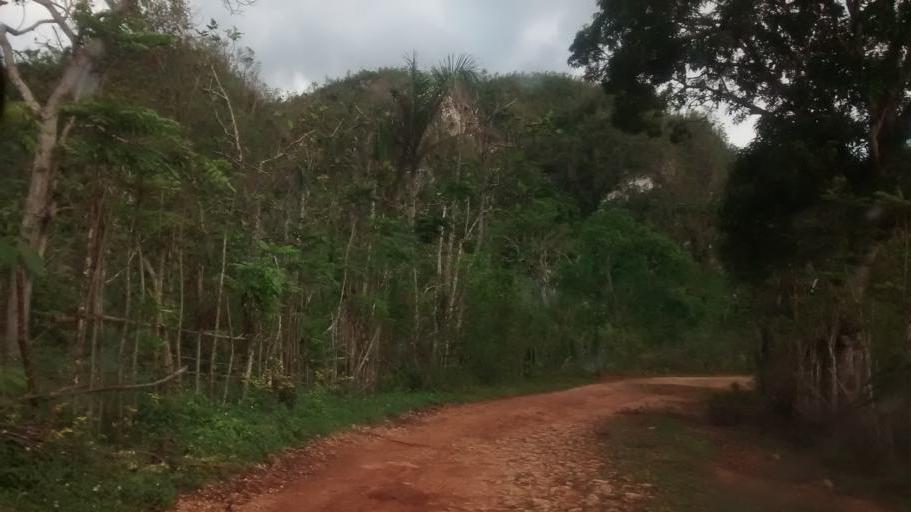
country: HT
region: Grandans
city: Corail
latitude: 18.5171
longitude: -73.7853
